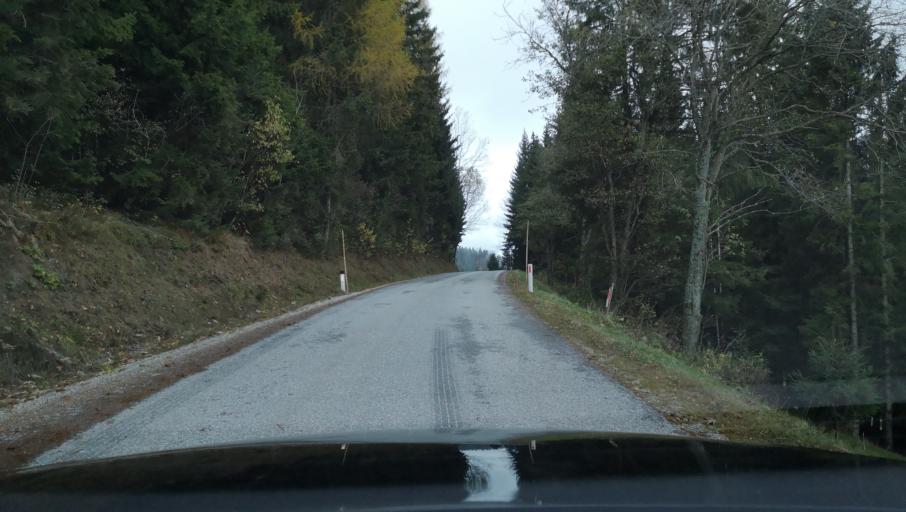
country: AT
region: Styria
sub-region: Politischer Bezirk Weiz
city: Gasen
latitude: 47.3531
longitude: 15.5921
